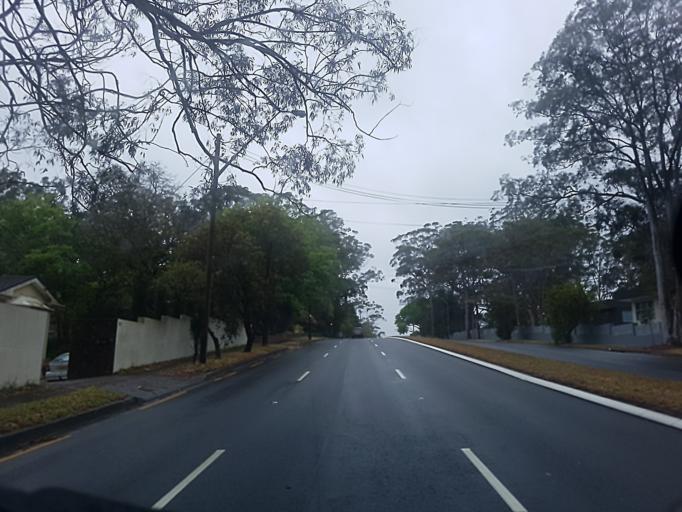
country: AU
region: New South Wales
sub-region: City of Sydney
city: Pymble
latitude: -33.7350
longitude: 151.1534
